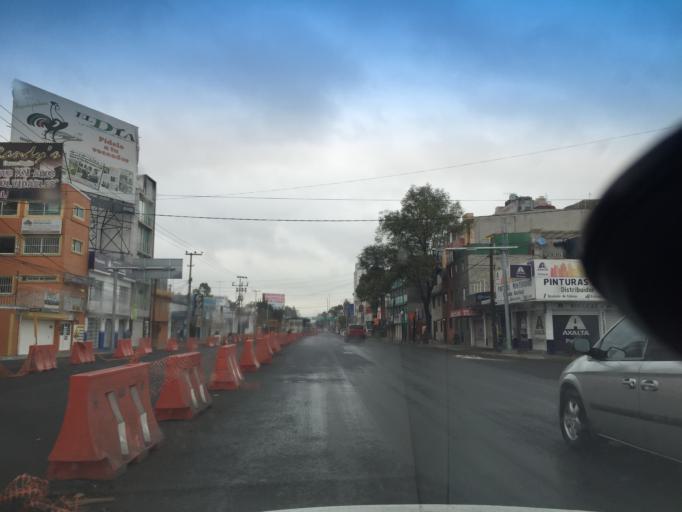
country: MX
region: Mexico
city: Colonia Lindavista
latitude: 19.4928
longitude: -99.1431
